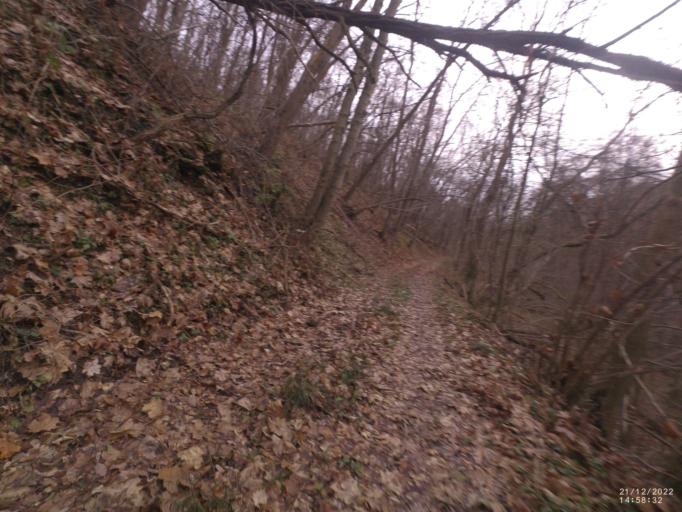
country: DE
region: Rheinland-Pfalz
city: Sinzig
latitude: 50.5276
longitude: 7.2566
